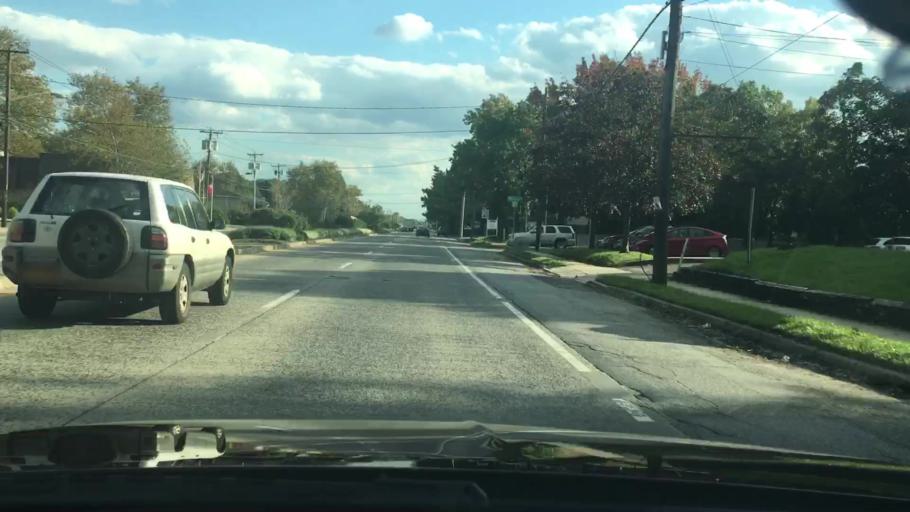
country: US
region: New York
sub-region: Suffolk County
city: Deer Park
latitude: 40.7717
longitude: -73.3336
